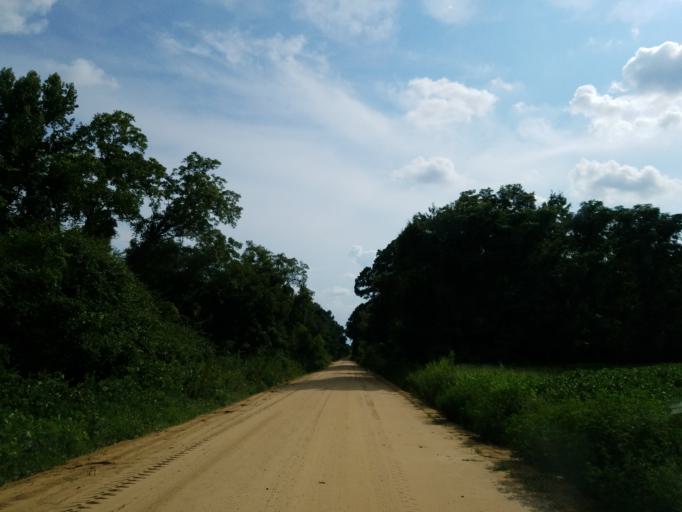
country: US
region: Georgia
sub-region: Dooly County
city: Unadilla
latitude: 32.1897
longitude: -83.7391
